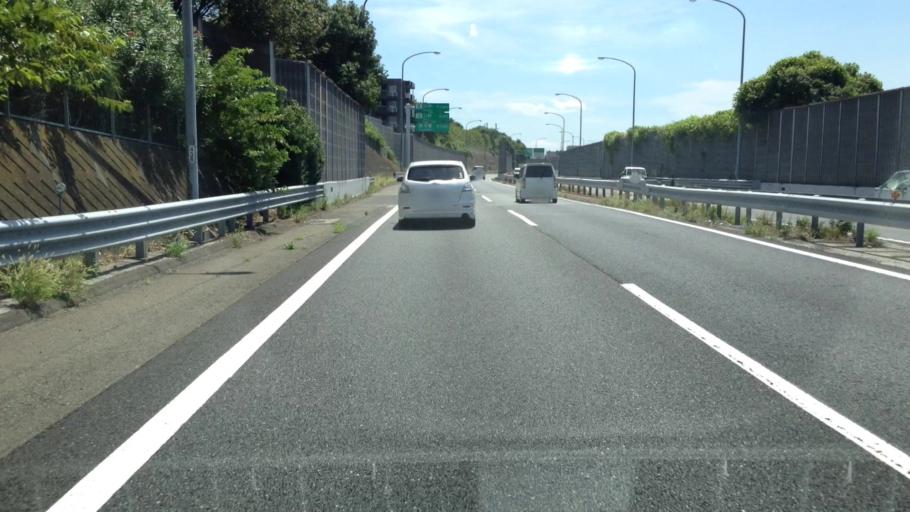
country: JP
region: Kanagawa
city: Yokohama
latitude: 35.4307
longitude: 139.5824
